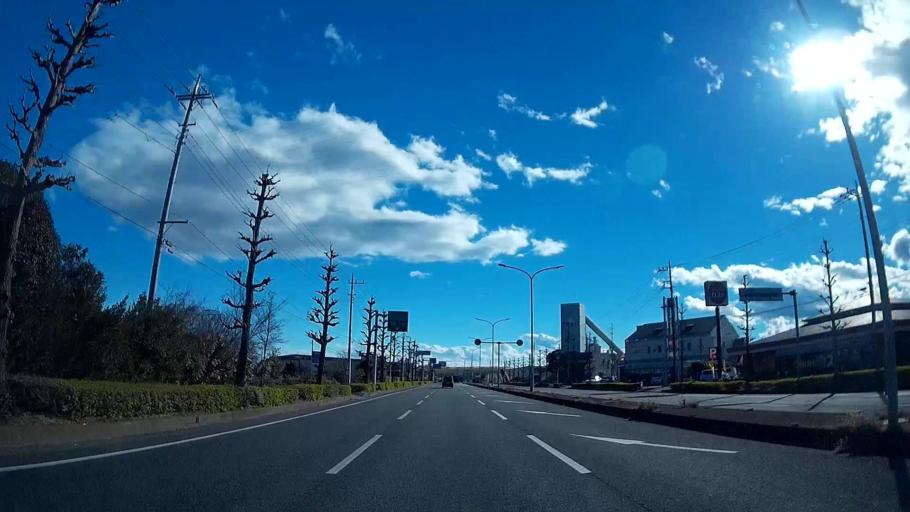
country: JP
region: Saitama
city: Yorii
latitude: 36.1238
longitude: 139.2055
